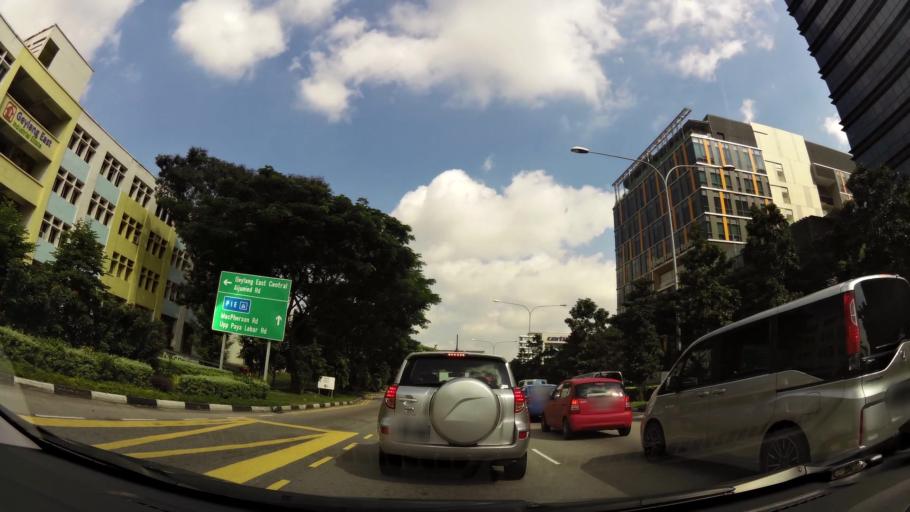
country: SG
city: Singapore
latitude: 1.3188
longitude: 103.8917
